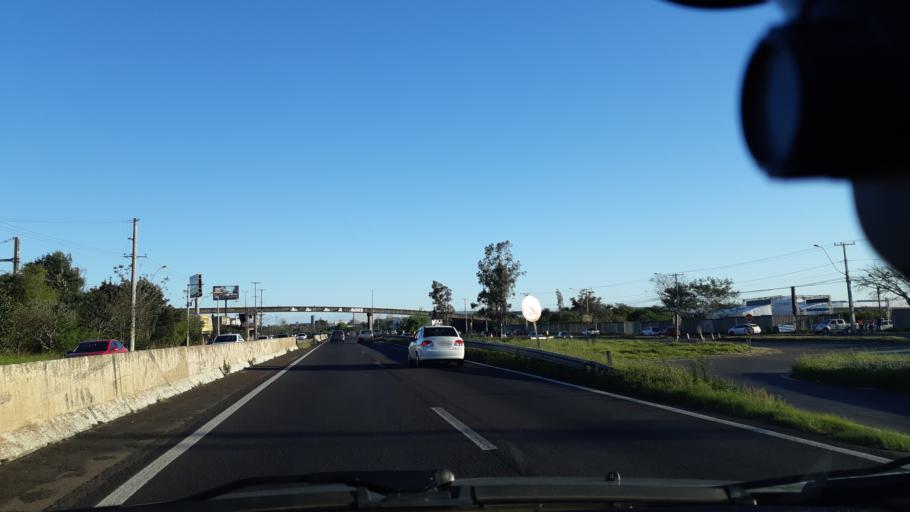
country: BR
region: Rio Grande do Sul
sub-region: Esteio
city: Esteio
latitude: -29.8576
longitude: -51.1806
